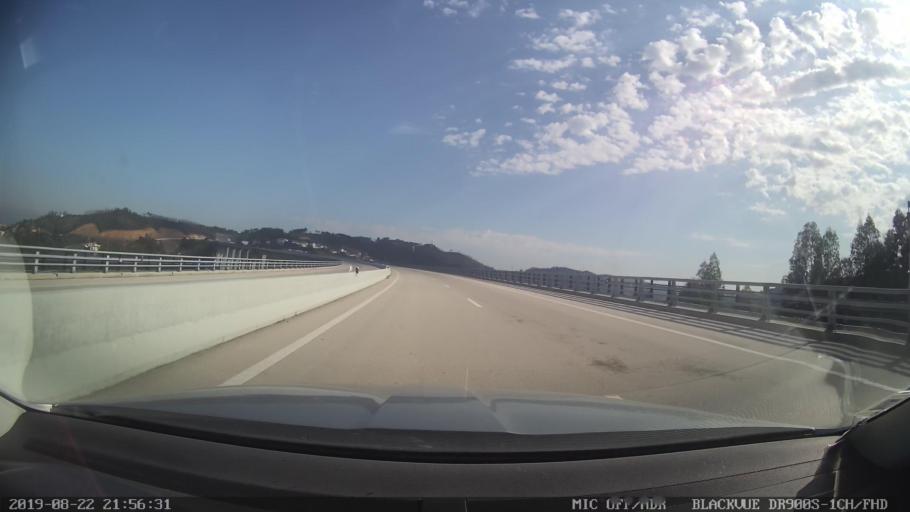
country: PT
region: Coimbra
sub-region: Coimbra
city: Coimbra
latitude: 40.1715
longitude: -8.3775
